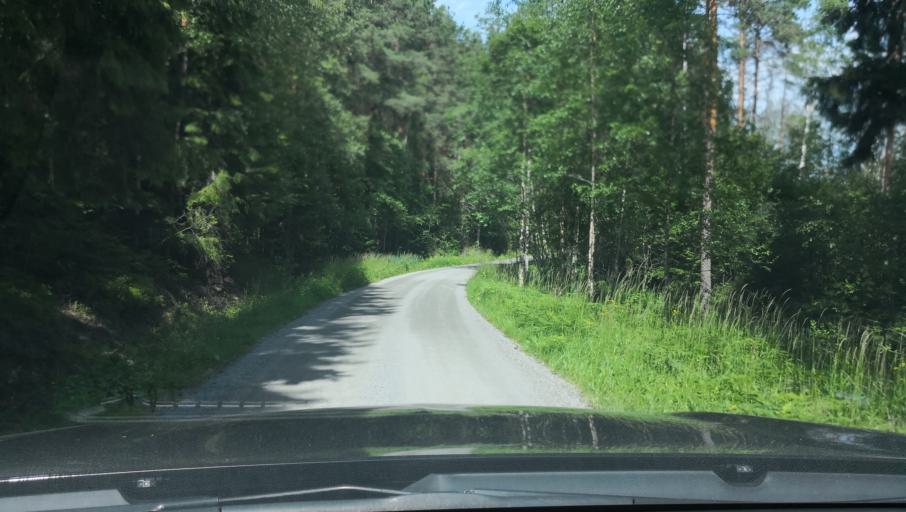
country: SE
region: Vaestmanland
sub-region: Surahammars Kommun
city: Ramnas
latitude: 59.8831
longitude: 16.0910
